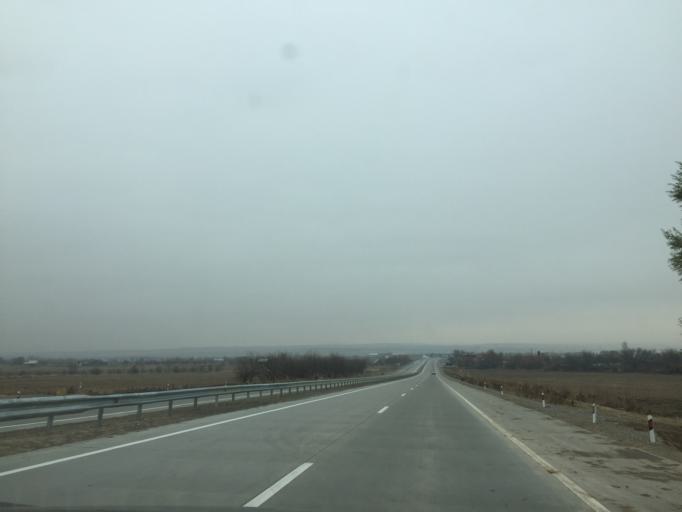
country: KZ
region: Ongtustik Qazaqstan
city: Aksu
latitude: 42.4699
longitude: 69.8003
